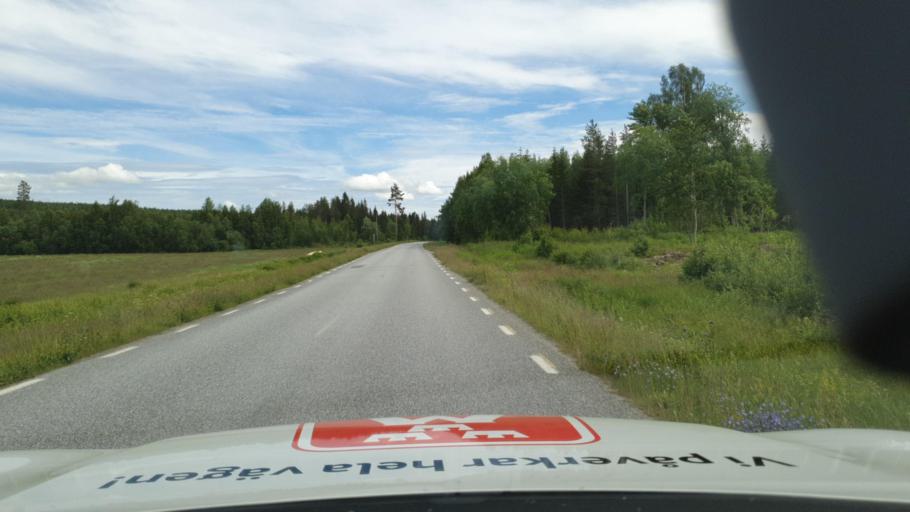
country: SE
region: Vaesterbotten
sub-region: Skelleftea Kommun
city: Soedra Bergsbyn
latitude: 64.5152
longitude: 20.9901
